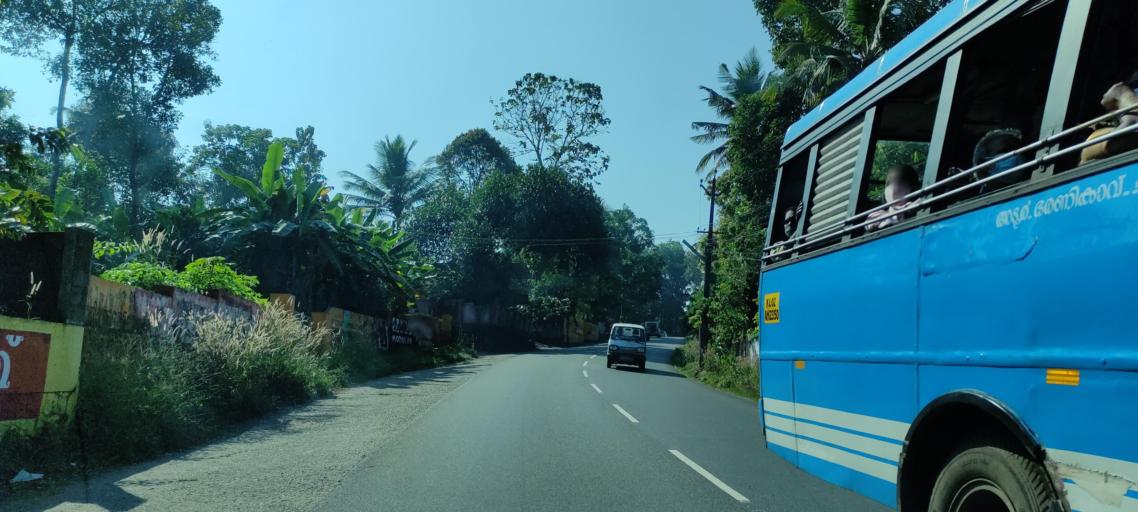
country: IN
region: Kerala
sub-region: Pattanamtitta
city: Adur
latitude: 9.1205
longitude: 76.7005
